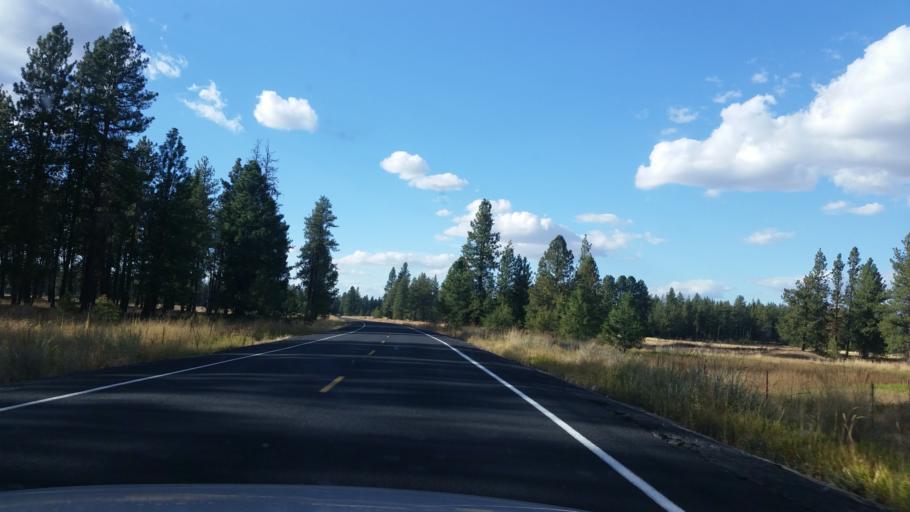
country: US
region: Washington
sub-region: Spokane County
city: Cheney
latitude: 47.4342
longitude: -117.5692
